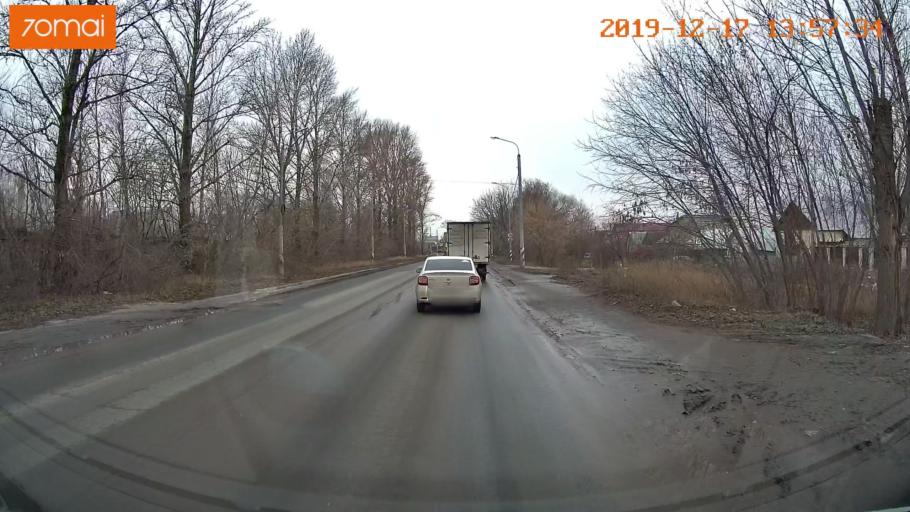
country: RU
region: Rjazan
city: Ryazan'
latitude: 54.6254
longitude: 39.6898
